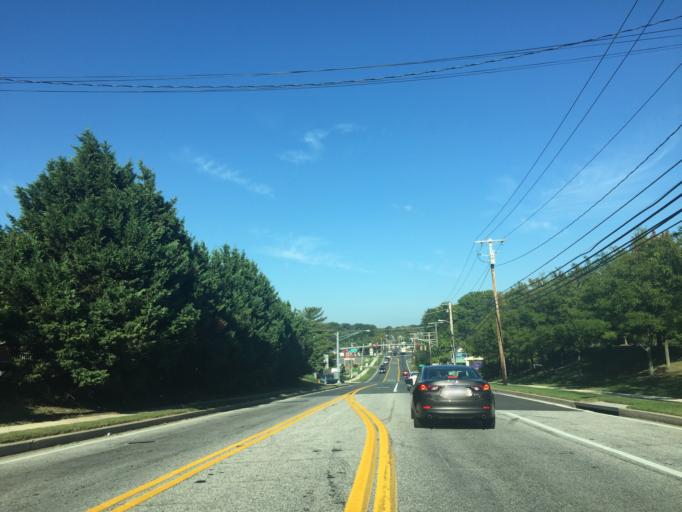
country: US
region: Maryland
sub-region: Baltimore County
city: Rossville
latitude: 39.3537
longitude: -76.4635
